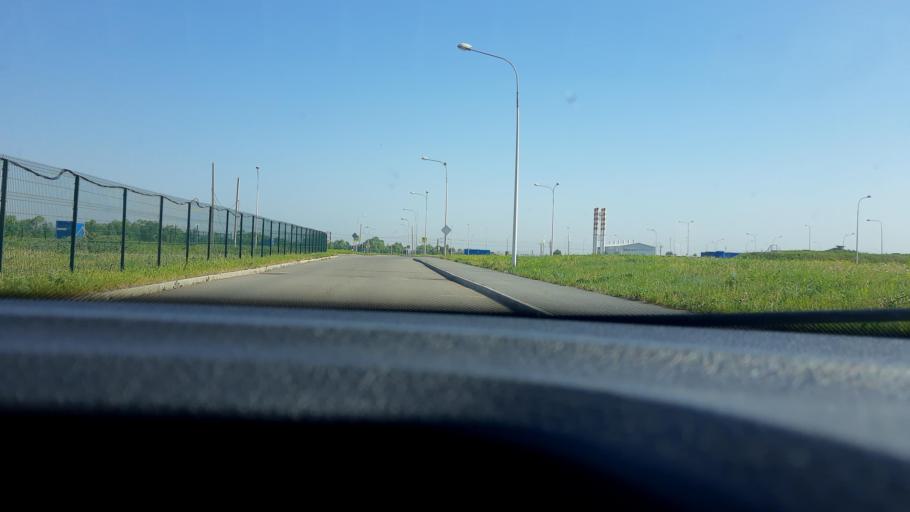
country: RU
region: Bashkortostan
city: Ufa
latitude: 54.6024
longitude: 55.9016
